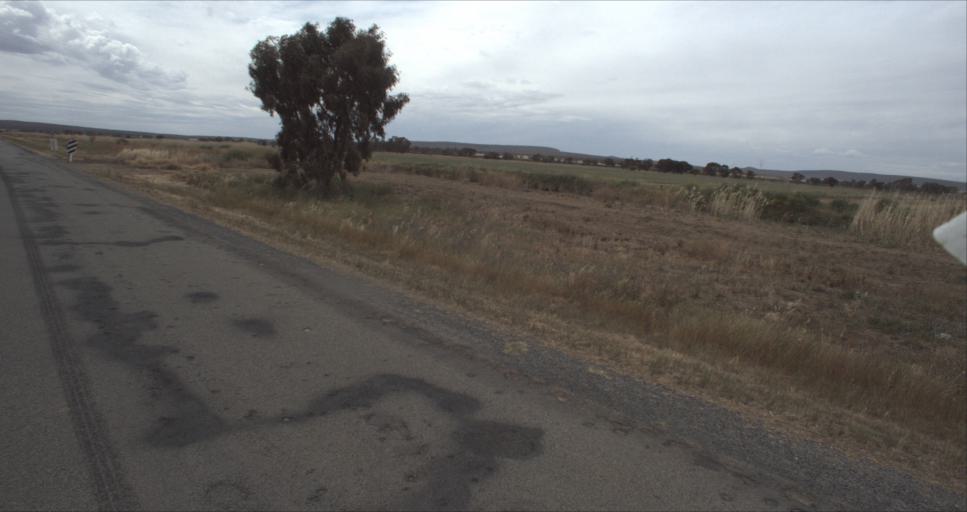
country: AU
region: New South Wales
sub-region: Leeton
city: Leeton
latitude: -34.4950
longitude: 146.4007
